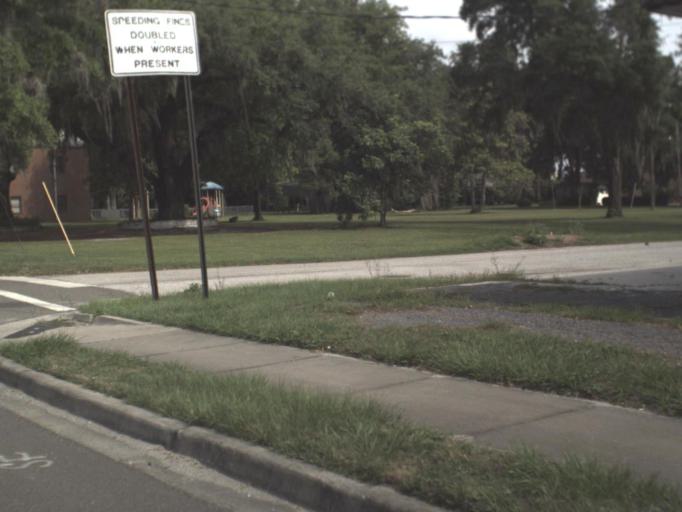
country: US
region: Florida
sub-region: Clay County
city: Green Cove Springs
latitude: 30.0047
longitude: -81.6876
